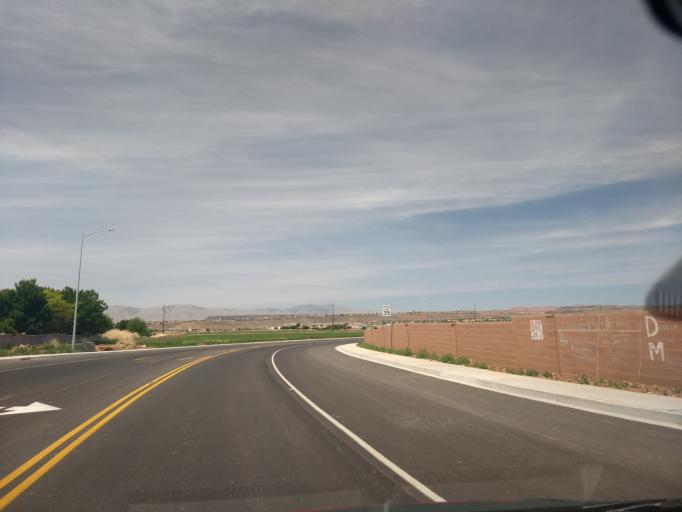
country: US
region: Utah
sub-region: Washington County
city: Washington
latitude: 37.0944
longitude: -113.5047
